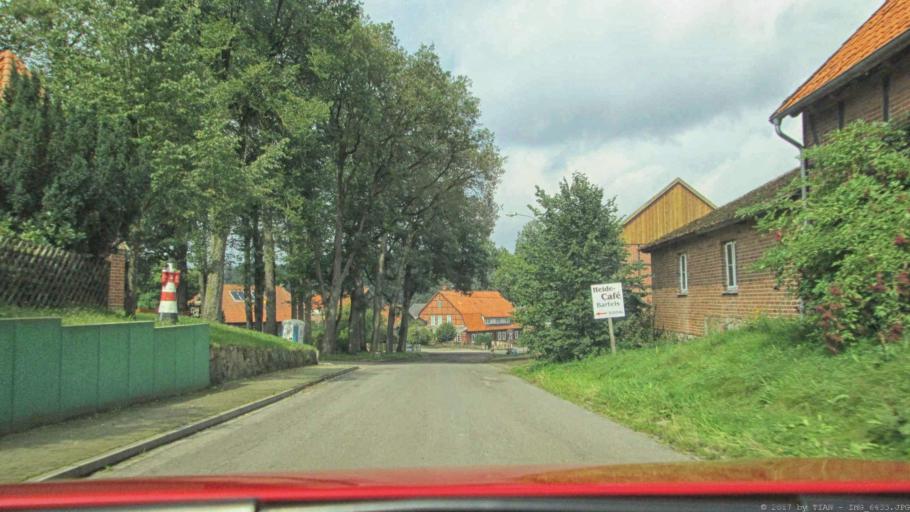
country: DE
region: Lower Saxony
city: Obernholz
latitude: 52.8070
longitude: 10.5474
